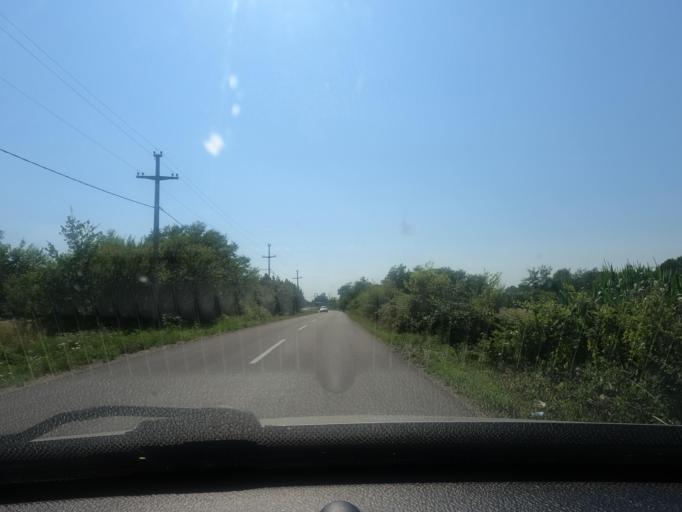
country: RS
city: Kozjak
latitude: 44.5464
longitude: 19.2940
